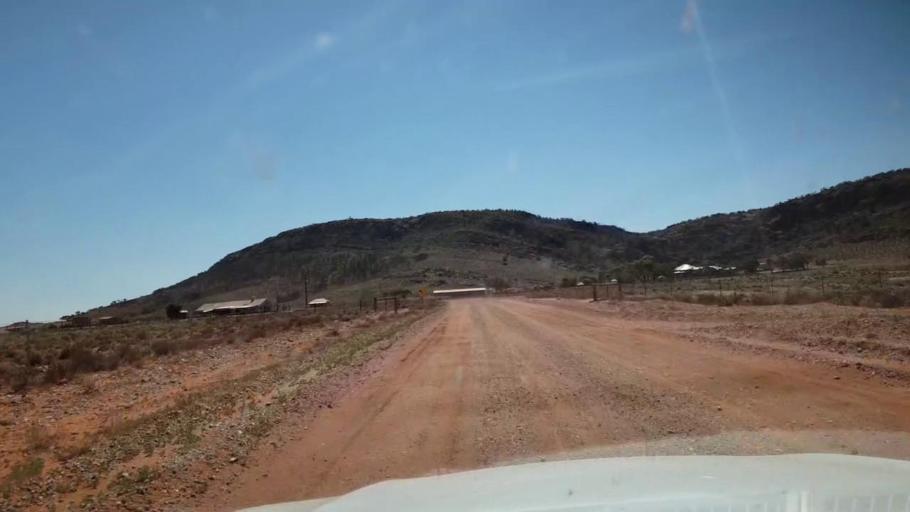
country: AU
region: South Australia
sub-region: Whyalla
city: Whyalla
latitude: -32.6874
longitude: 137.1265
